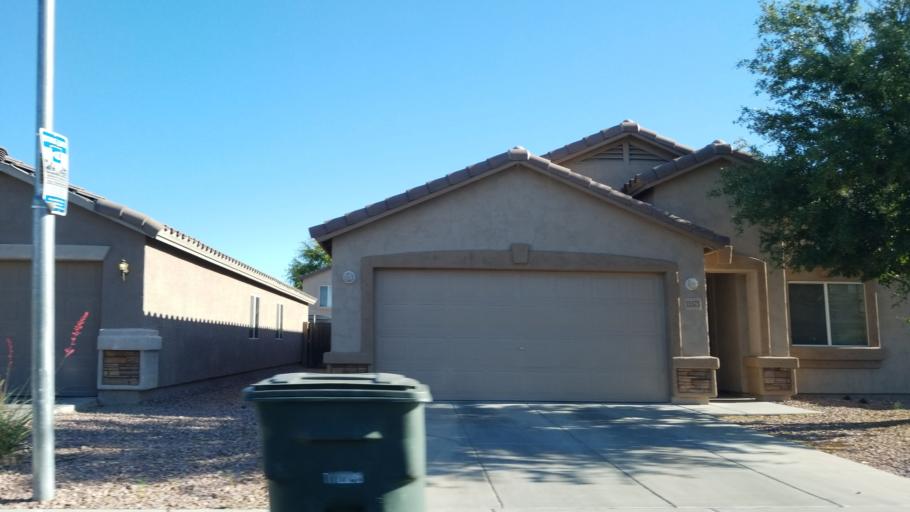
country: US
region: Arizona
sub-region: Maricopa County
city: Youngtown
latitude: 33.5780
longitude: -112.3087
